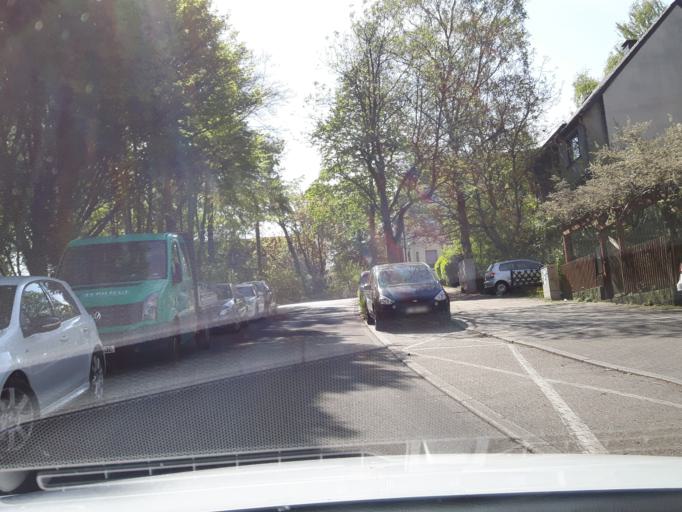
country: DE
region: North Rhine-Westphalia
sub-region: Regierungsbezirk Dusseldorf
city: Essen
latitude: 51.4243
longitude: 7.0294
